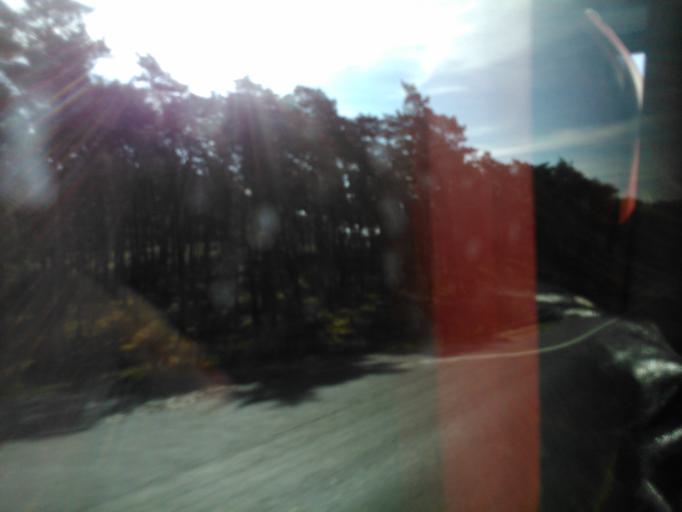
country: PL
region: Kujawsko-Pomorskie
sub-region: Powiat aleksandrowski
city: Aleksandrow Kujawski
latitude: 52.9408
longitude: 18.6994
